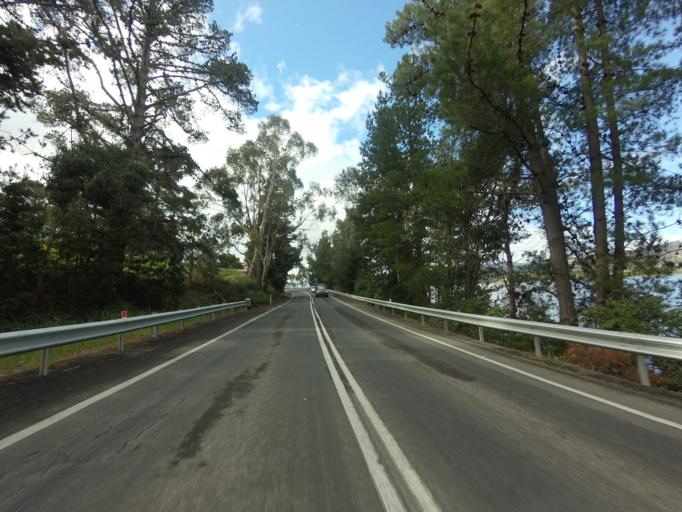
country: AU
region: Tasmania
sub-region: Huon Valley
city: Geeveston
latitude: -43.1535
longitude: 146.9805
